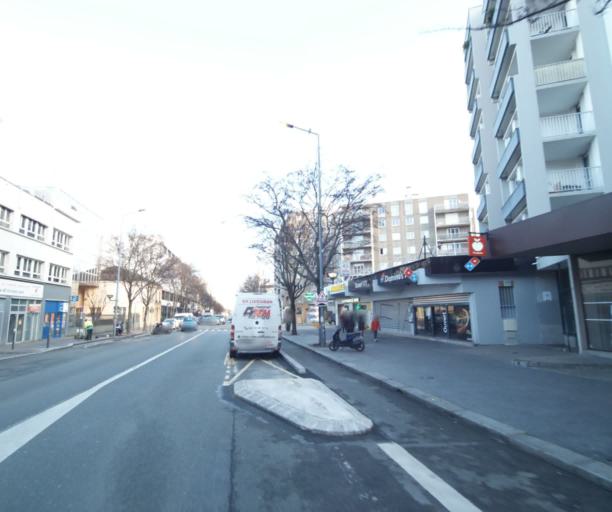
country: FR
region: Ile-de-France
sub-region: Paris
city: Saint-Ouen
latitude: 48.9031
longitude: 2.3308
